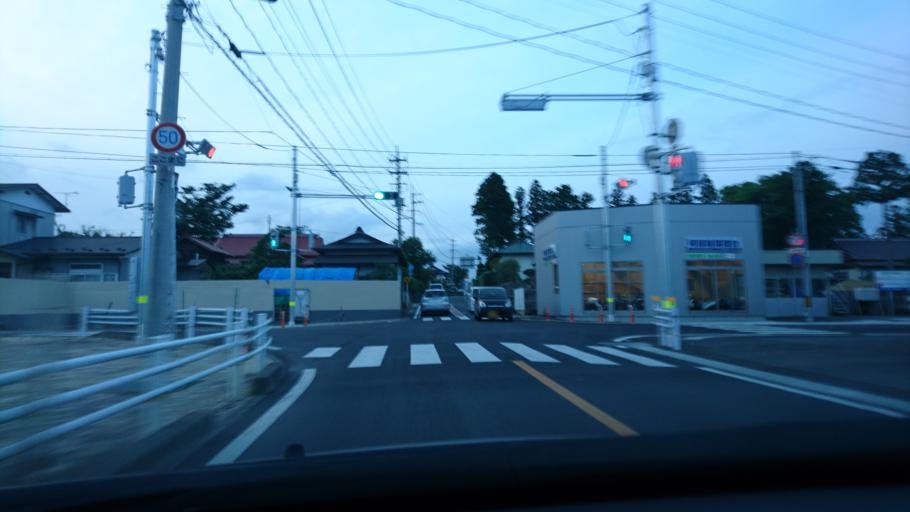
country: JP
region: Iwate
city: Ichinoseki
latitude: 38.8091
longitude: 140.9836
